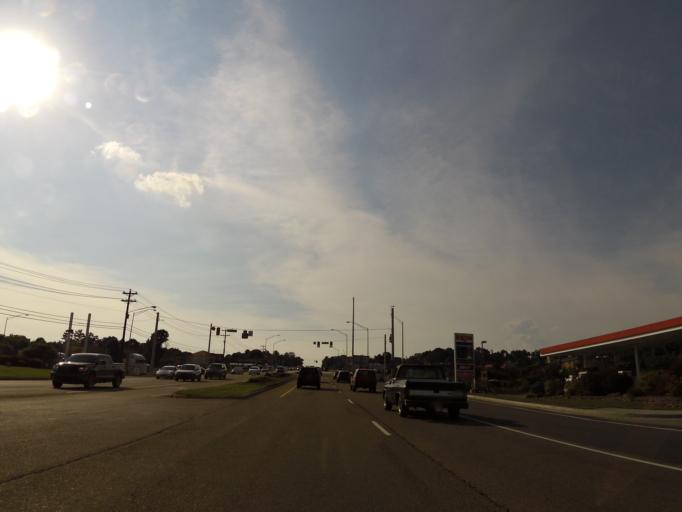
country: US
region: Tennessee
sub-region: Loudon County
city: Lenoir City
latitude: 35.8275
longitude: -84.2777
